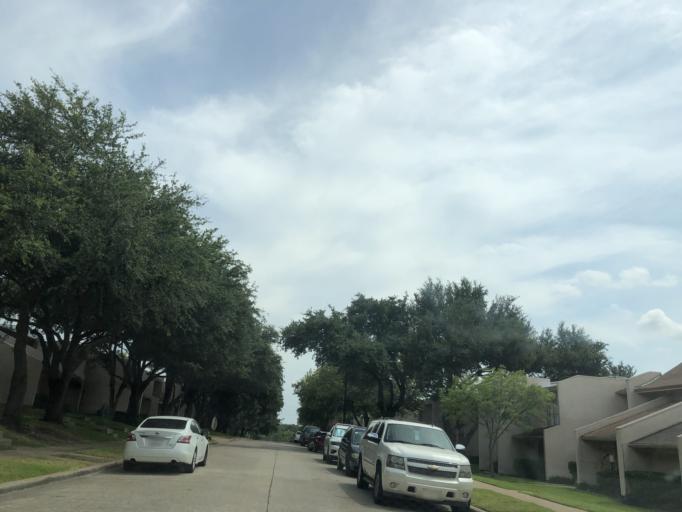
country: US
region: Texas
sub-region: Dallas County
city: Garland
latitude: 32.8660
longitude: -96.6344
